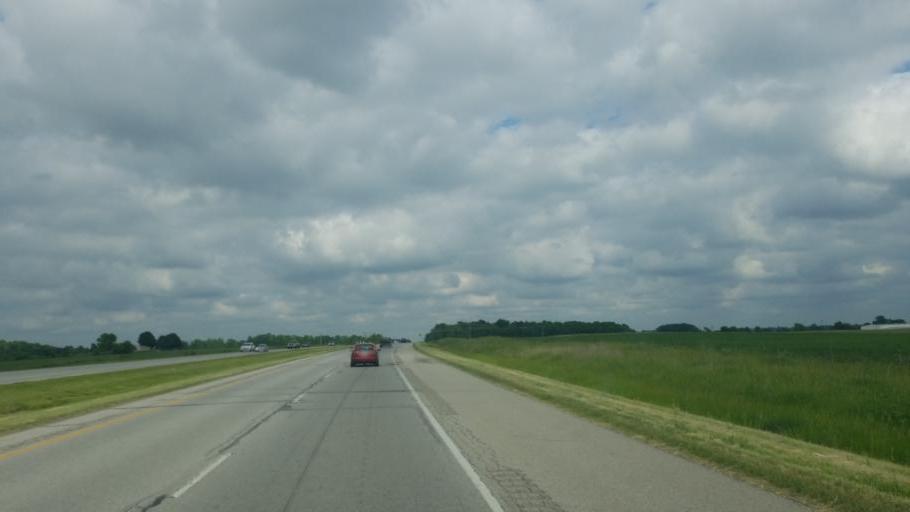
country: US
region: Indiana
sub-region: Kosciusko County
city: Warsaw
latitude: 41.2686
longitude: -85.9473
